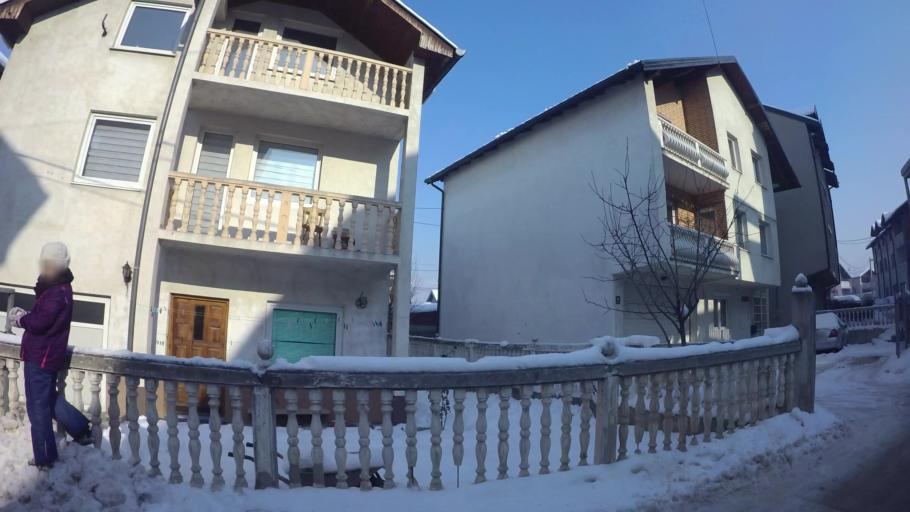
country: BA
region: Federation of Bosnia and Herzegovina
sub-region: Kanton Sarajevo
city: Sarajevo
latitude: 43.8448
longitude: 18.3865
